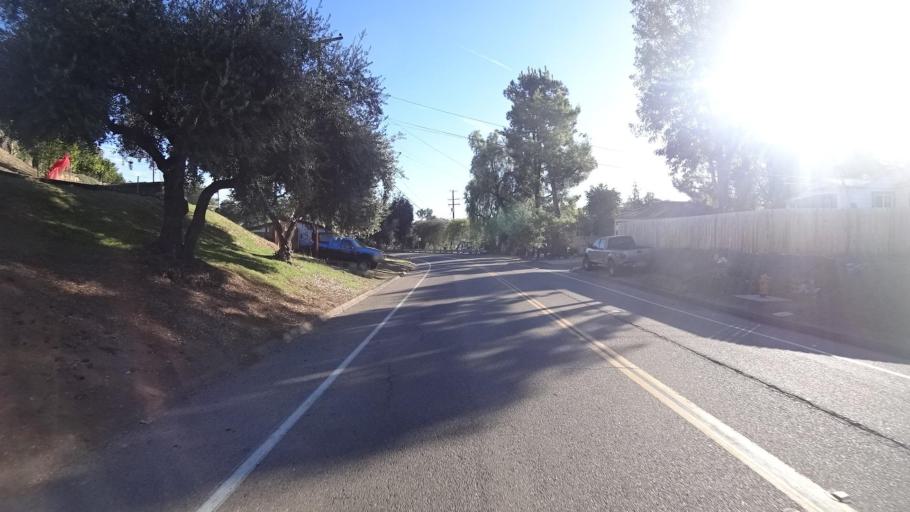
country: US
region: California
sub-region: San Diego County
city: Lakeside
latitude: 32.8369
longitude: -116.9064
